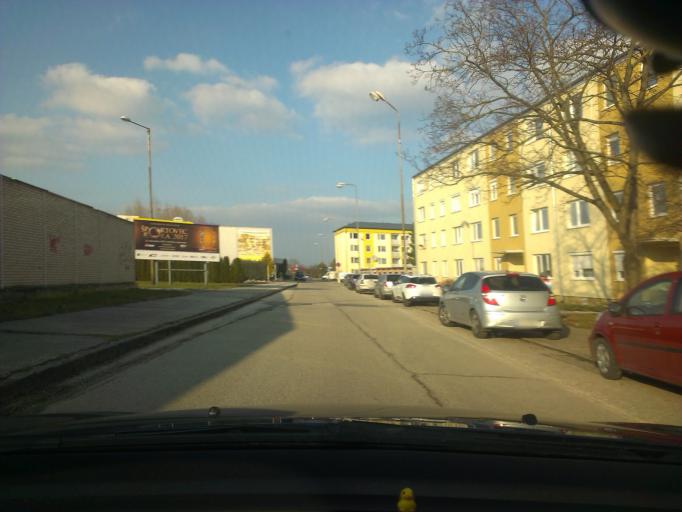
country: SK
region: Trnavsky
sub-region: Okres Trnava
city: Piestany
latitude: 48.5974
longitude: 17.8172
